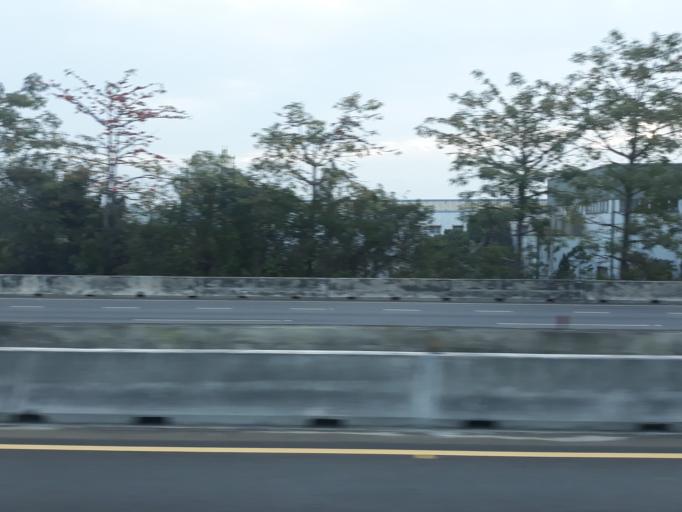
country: TW
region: Taiwan
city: Fengyuan
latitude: 24.2765
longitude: 120.6935
